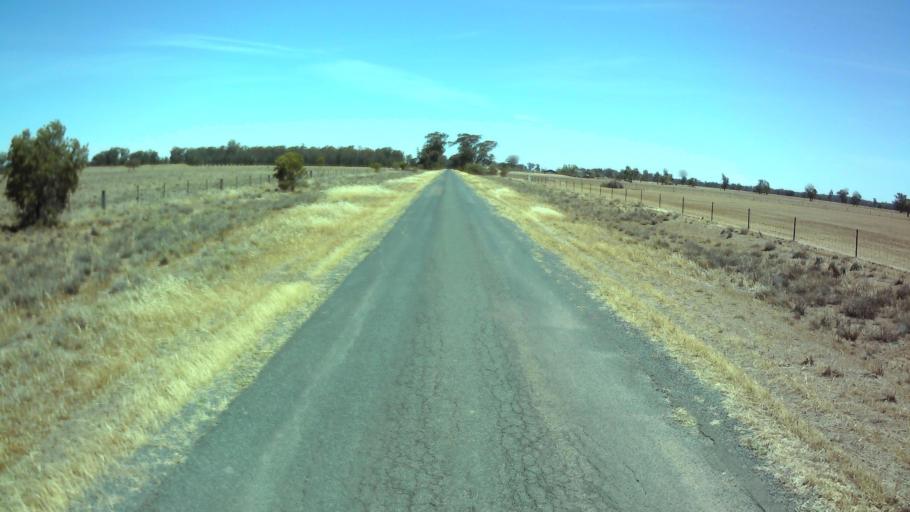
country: AU
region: New South Wales
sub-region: Weddin
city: Grenfell
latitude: -33.8972
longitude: 147.6870
